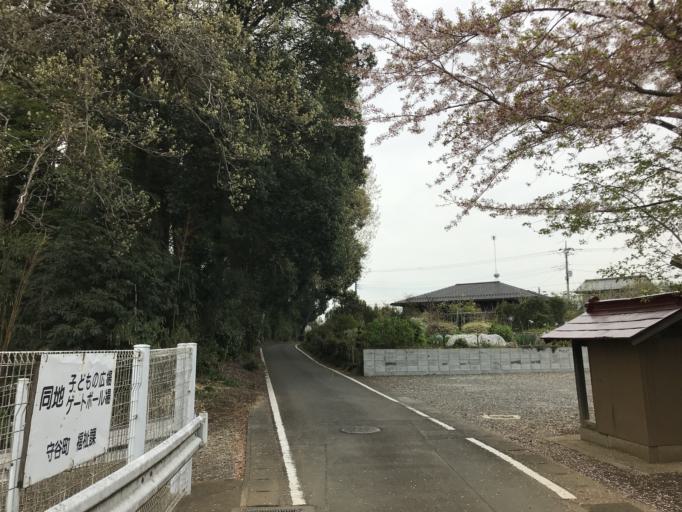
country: JP
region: Ibaraki
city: Moriya
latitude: 35.9530
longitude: 140.0144
